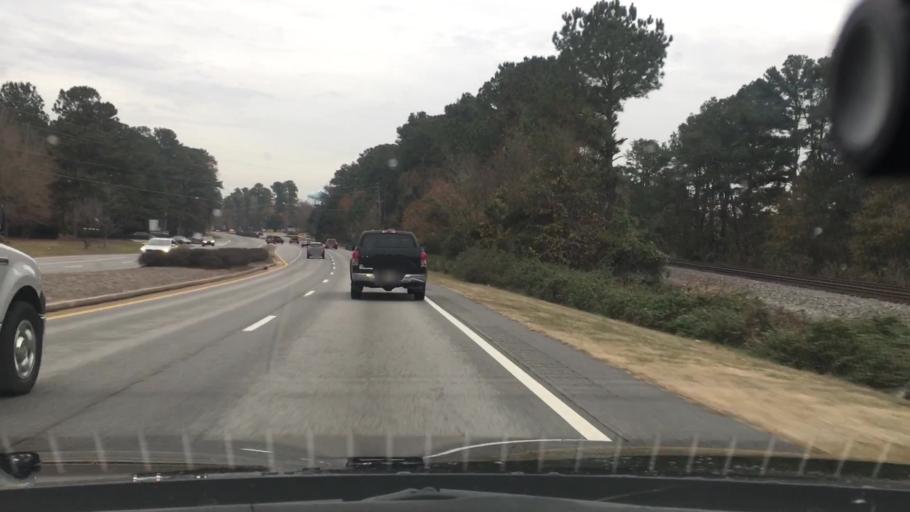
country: US
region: Georgia
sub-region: Fayette County
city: Peachtree City
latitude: 33.4035
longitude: -84.5989
